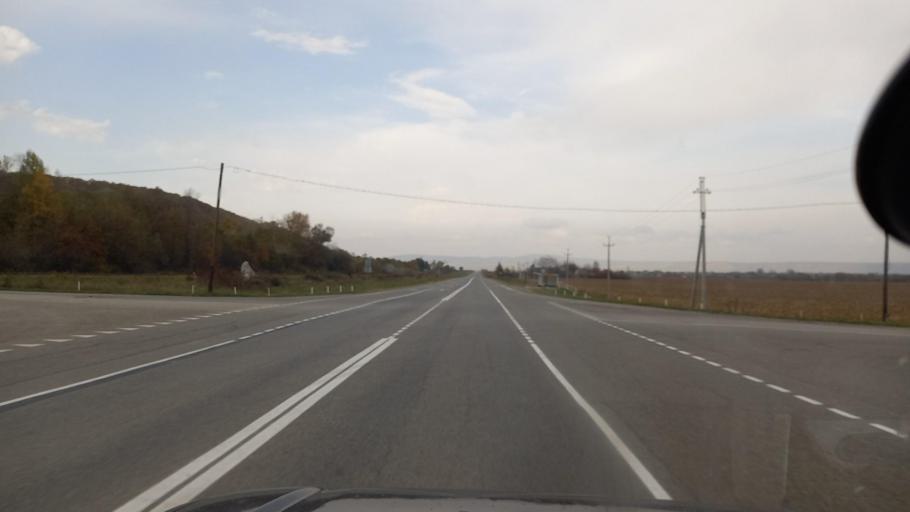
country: RU
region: Krasnodarskiy
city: Shedok
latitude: 44.2369
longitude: 40.8588
